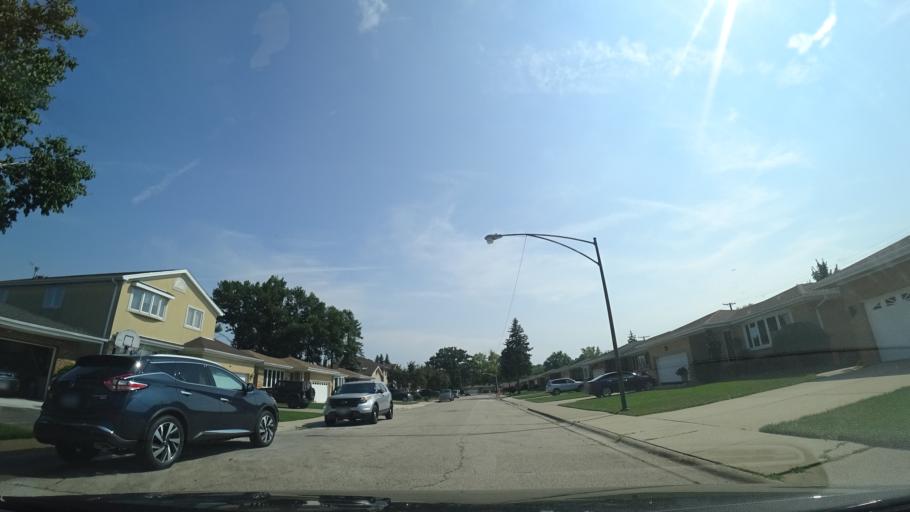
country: US
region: Illinois
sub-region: Cook County
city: Norridge
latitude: 41.9628
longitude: -87.8417
